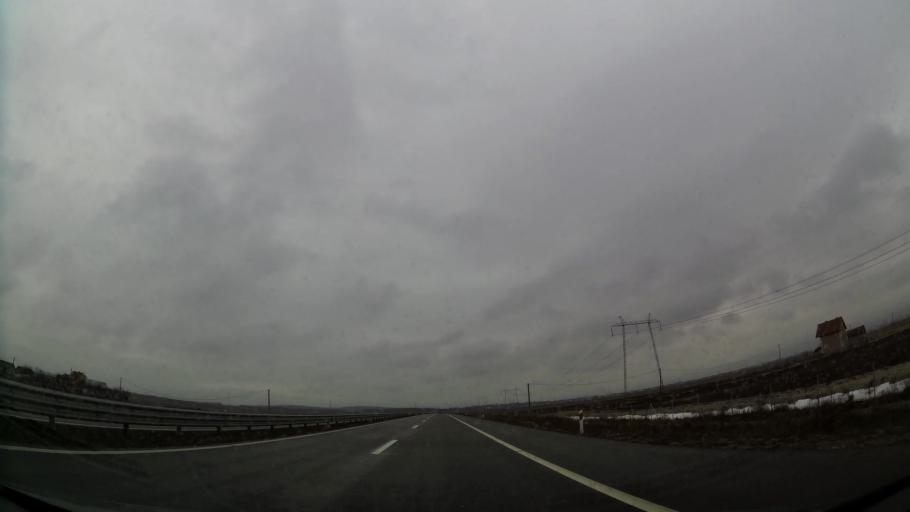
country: XK
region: Ferizaj
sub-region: Komuna e Ferizajt
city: Ferizaj
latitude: 42.3952
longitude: 21.1991
